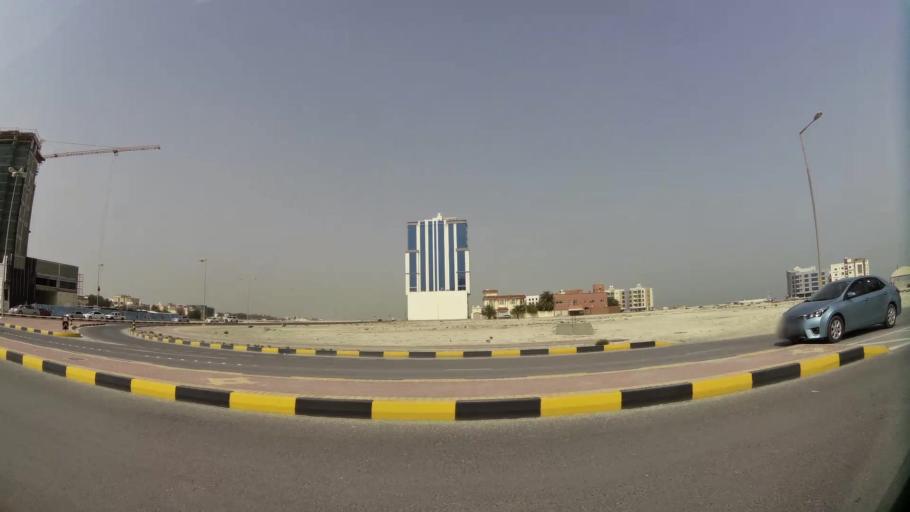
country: BH
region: Manama
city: Jidd Hafs
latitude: 26.2368
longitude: 50.5292
